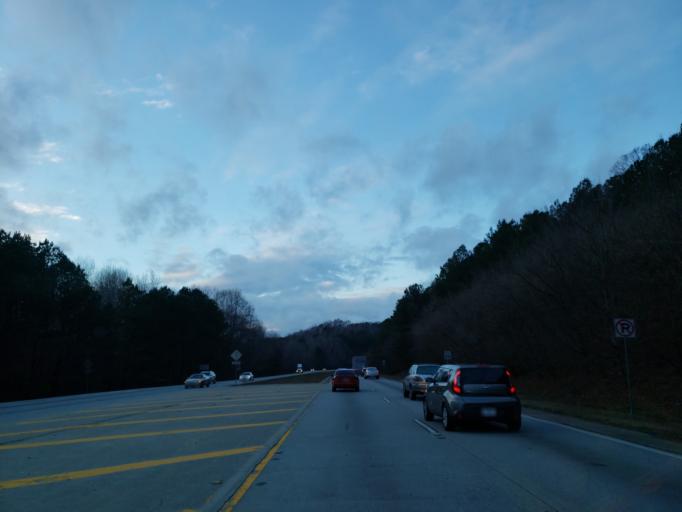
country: US
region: Georgia
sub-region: Fulton County
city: Union City
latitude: 33.6701
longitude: -84.5483
